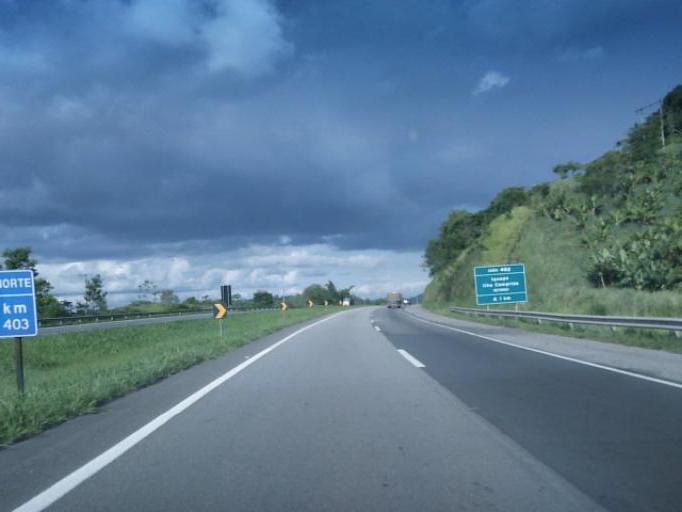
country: BR
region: Sao Paulo
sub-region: Miracatu
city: Miracatu
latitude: -24.3172
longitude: -47.5286
